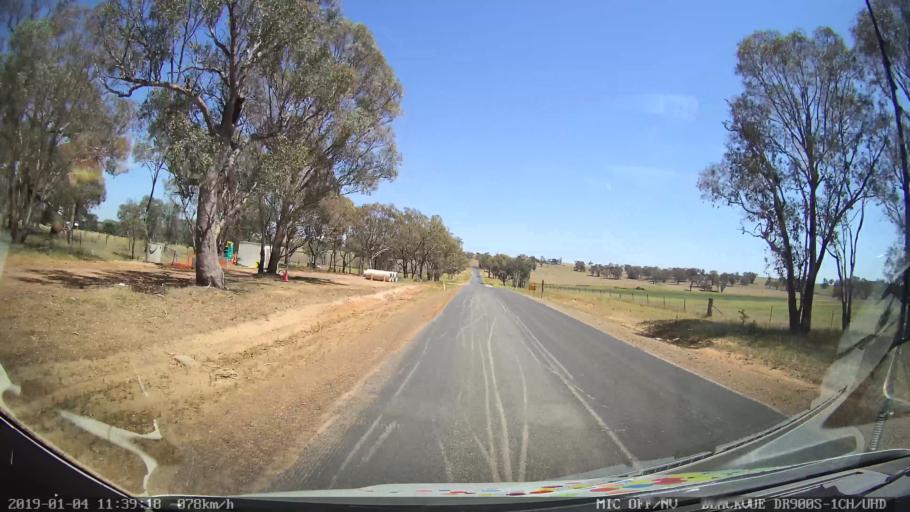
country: AU
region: New South Wales
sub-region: Cabonne
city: Molong
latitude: -33.0146
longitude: 148.7969
